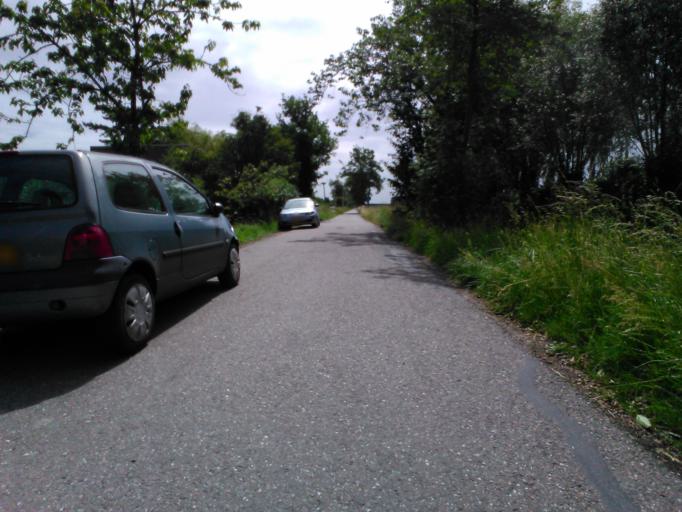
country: NL
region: South Holland
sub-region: Gemeente Alblasserdam
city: Alblasserdam
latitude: 51.8805
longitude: 4.6707
